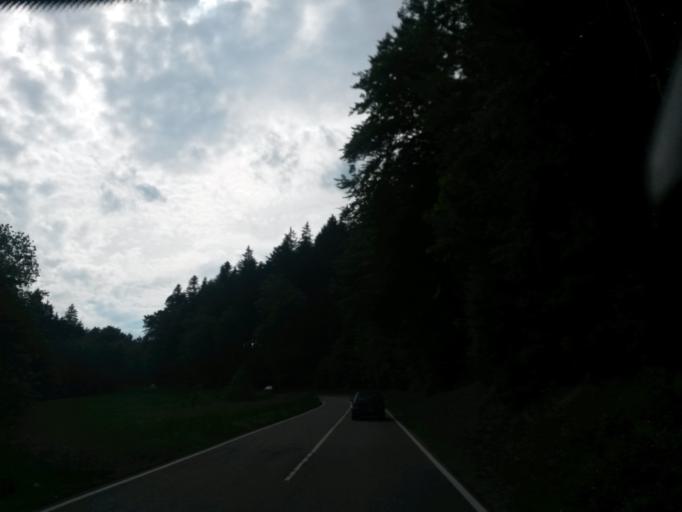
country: DE
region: Baden-Wuerttemberg
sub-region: Karlsruhe Region
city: Oberreichenbach
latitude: 48.7346
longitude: 8.6801
